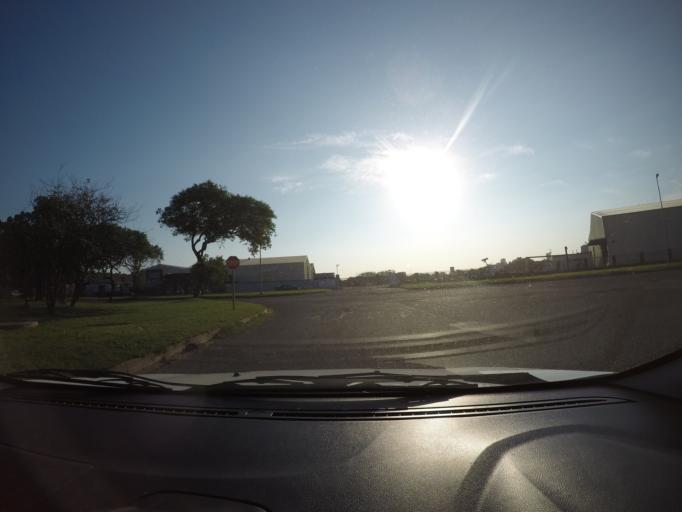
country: ZA
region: KwaZulu-Natal
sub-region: uThungulu District Municipality
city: Richards Bay
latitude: -28.7638
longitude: 32.0049
